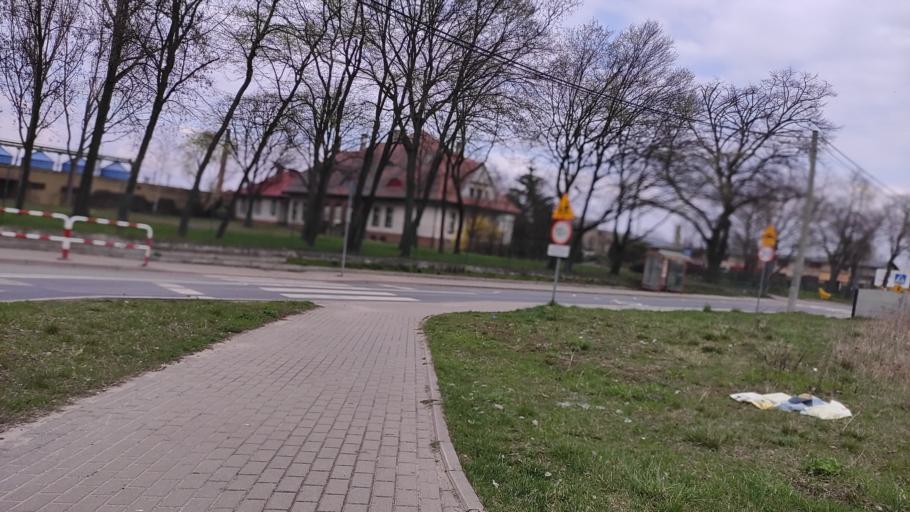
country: PL
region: Greater Poland Voivodeship
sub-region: Powiat poznanski
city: Kostrzyn
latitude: 52.4019
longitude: 17.1591
